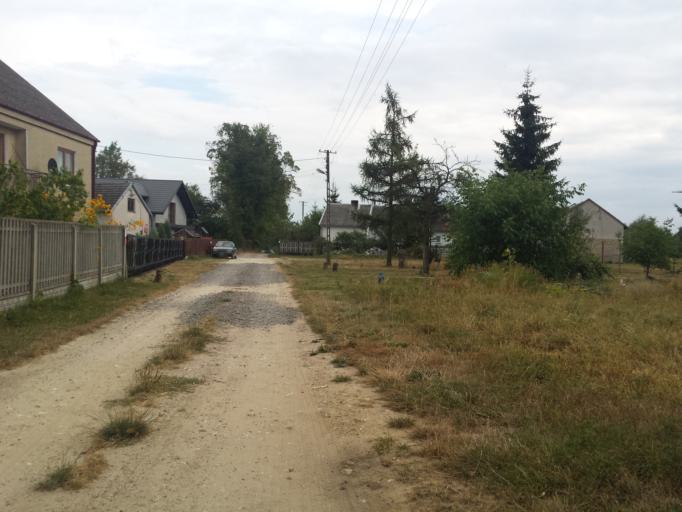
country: PL
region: Swietokrzyskie
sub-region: Powiat kielecki
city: Rakow
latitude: 50.6838
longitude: 21.0684
